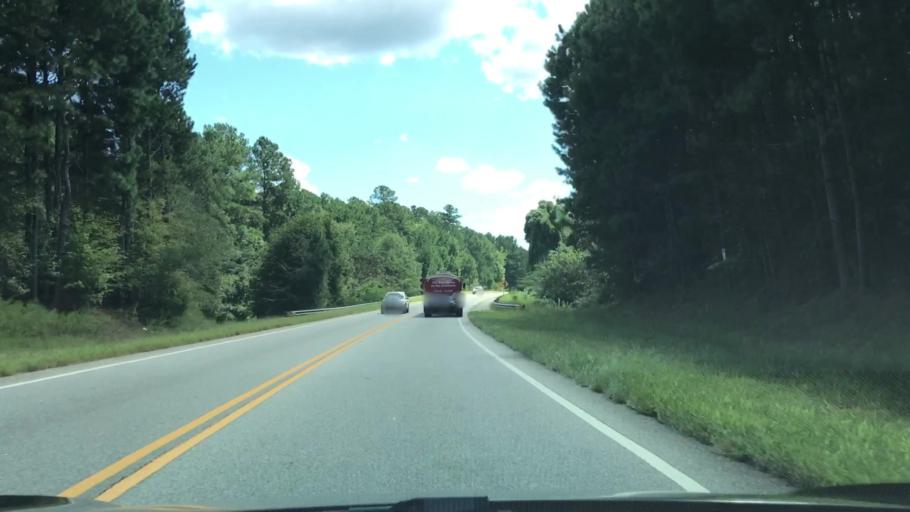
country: US
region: Georgia
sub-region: Greene County
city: Greensboro
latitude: 33.7168
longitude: -83.2922
